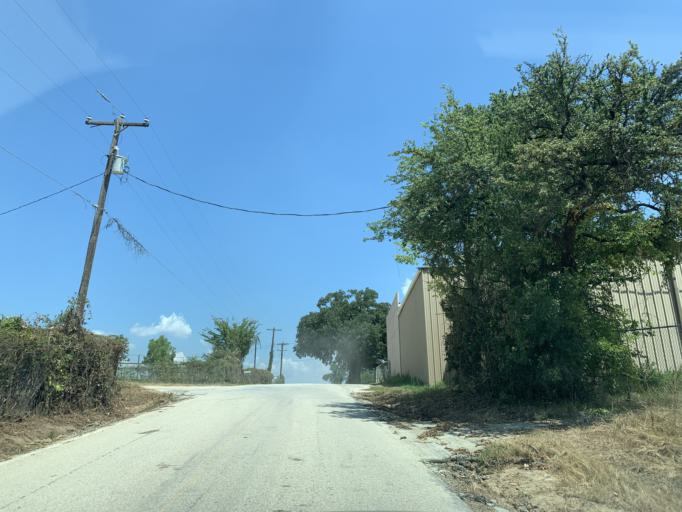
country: US
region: Texas
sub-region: Tarrant County
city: Lakeside
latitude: 32.8507
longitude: -97.5077
